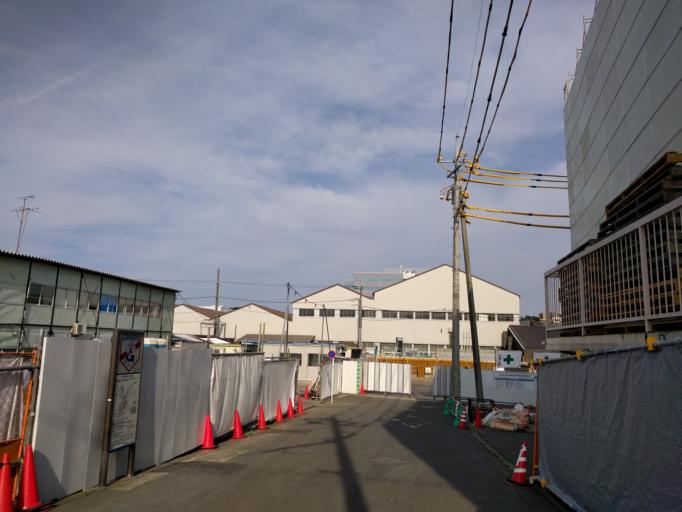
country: JP
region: Kanagawa
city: Kamakura
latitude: 35.3558
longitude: 139.5337
